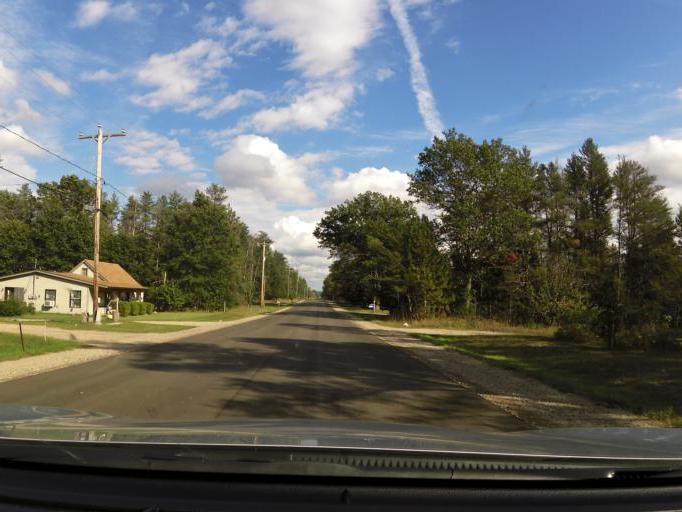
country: US
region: Michigan
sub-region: Roscommon County
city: Roscommon
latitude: 44.5256
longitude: -84.5652
